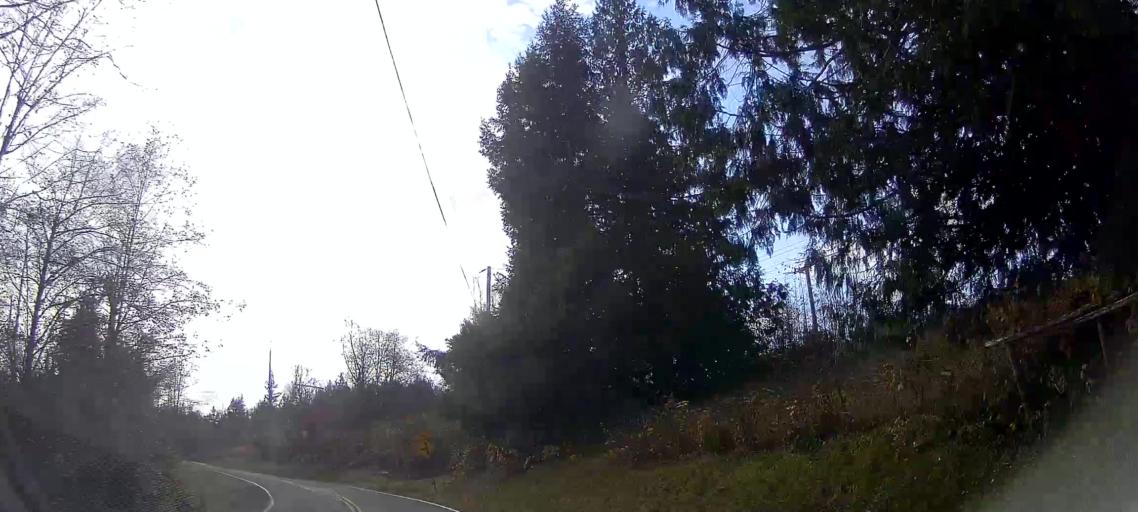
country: US
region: Washington
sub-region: Skagit County
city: Big Lake
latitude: 48.4119
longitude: -122.2128
